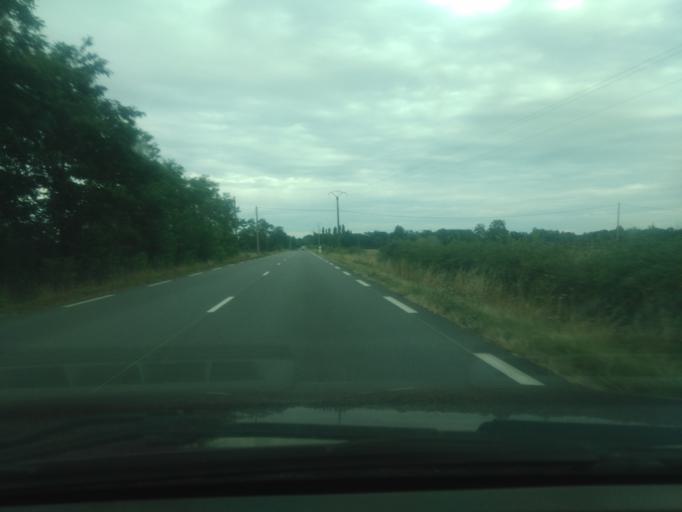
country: FR
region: Auvergne
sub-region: Departement de l'Allier
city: Ainay-le-Chateau
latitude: 46.7373
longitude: 2.6890
